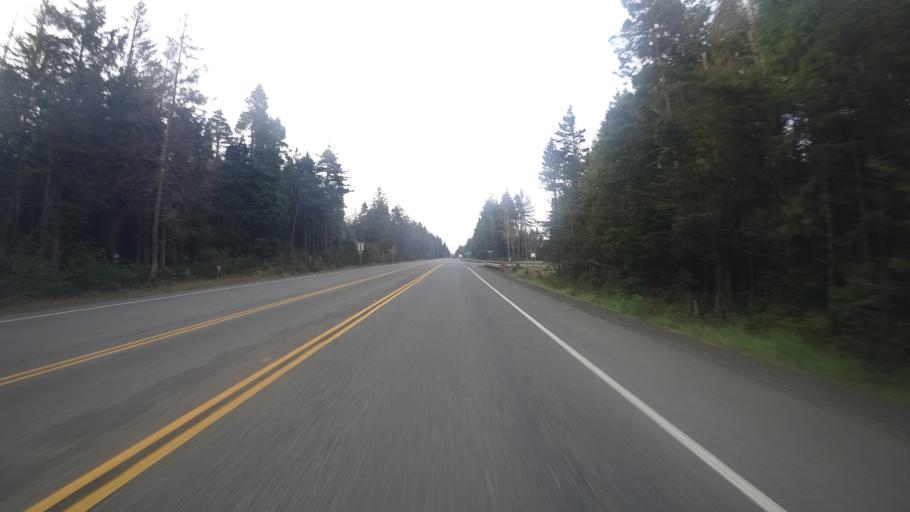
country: US
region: Oregon
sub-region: Coos County
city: Lakeside
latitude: 43.5164
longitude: -124.2170
